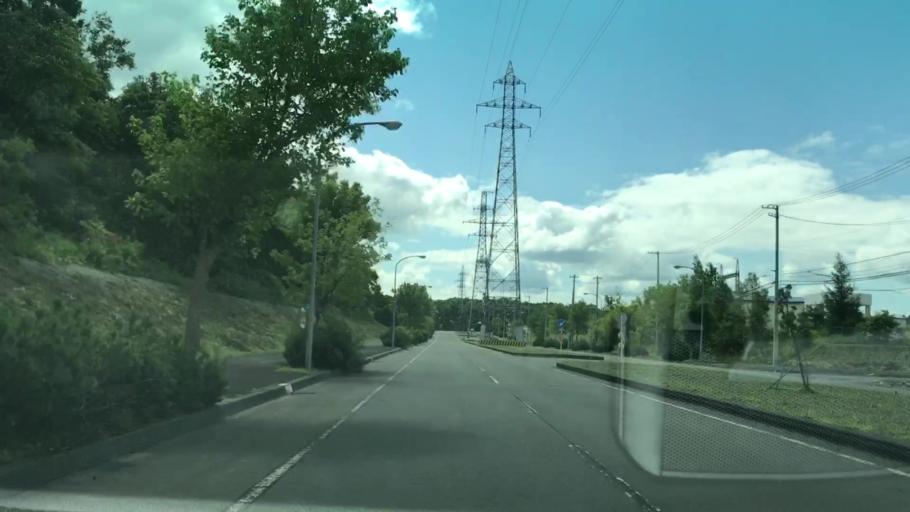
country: JP
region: Hokkaido
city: Chitose
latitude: 42.7760
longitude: 141.6166
